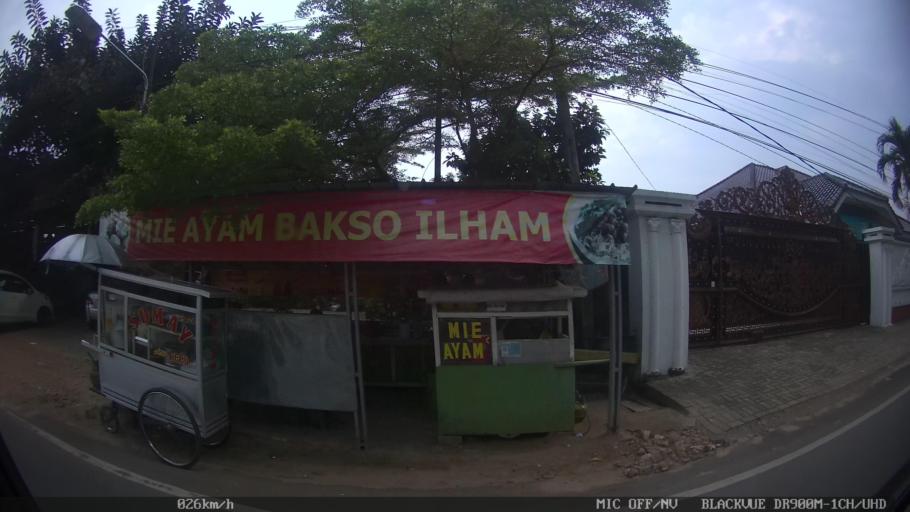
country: ID
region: Lampung
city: Bandarlampung
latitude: -5.4270
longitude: 105.2669
